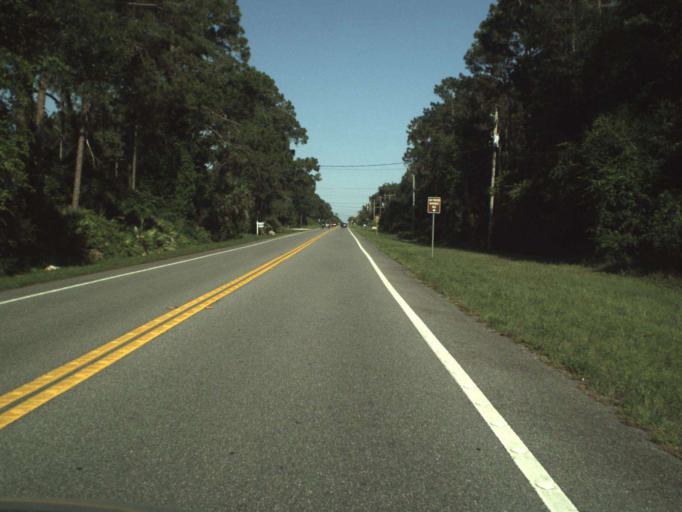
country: US
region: Florida
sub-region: Seminole County
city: Geneva
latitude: 28.7266
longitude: -81.1016
